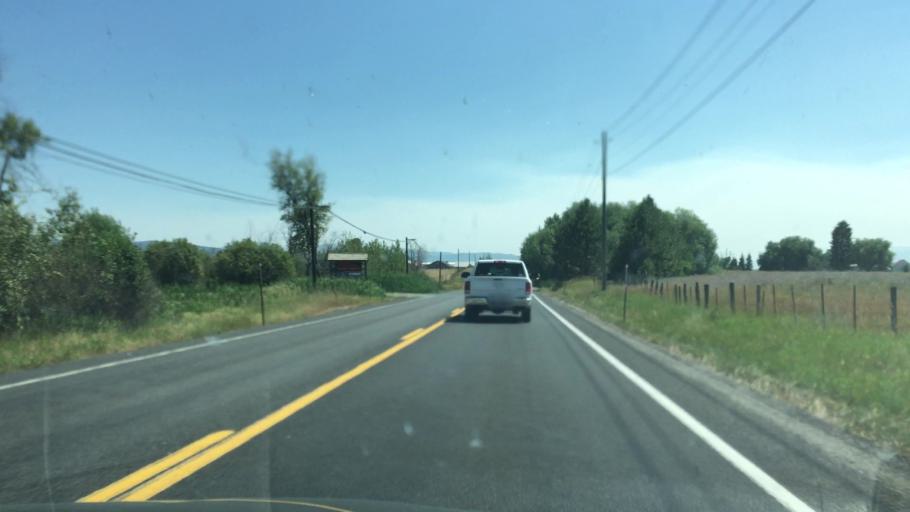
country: US
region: Idaho
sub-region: Valley County
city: McCall
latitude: 44.8442
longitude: -116.0885
